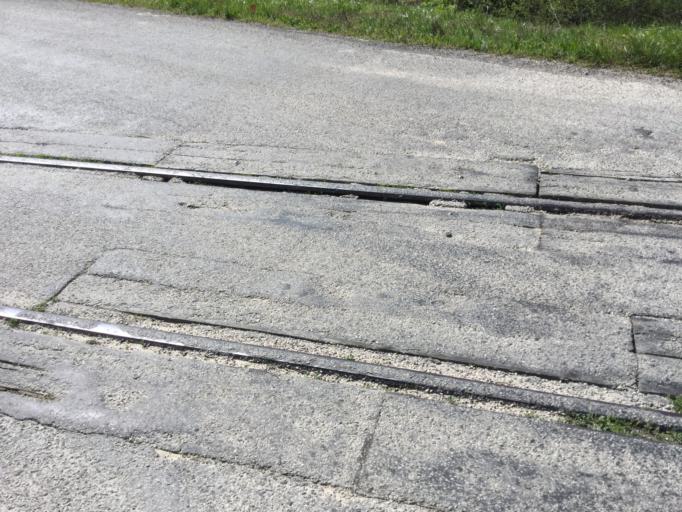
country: US
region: Kansas
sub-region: Neosho County
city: Chanute
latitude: 37.6601
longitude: -95.4982
